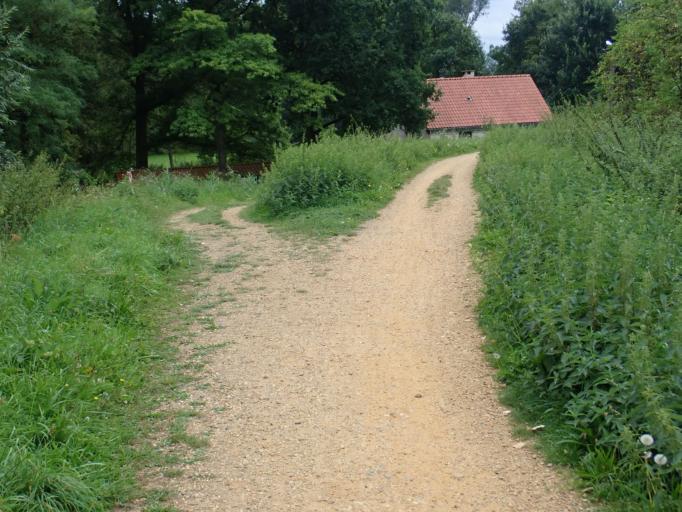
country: BE
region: Flanders
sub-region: Provincie Antwerpen
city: Niel
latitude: 51.0922
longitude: 4.3133
